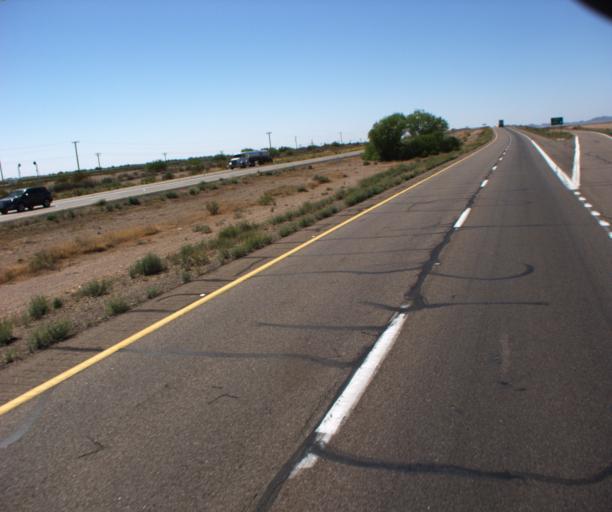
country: US
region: Arizona
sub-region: Maricopa County
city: Gila Bend
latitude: 32.9332
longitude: -112.7982
